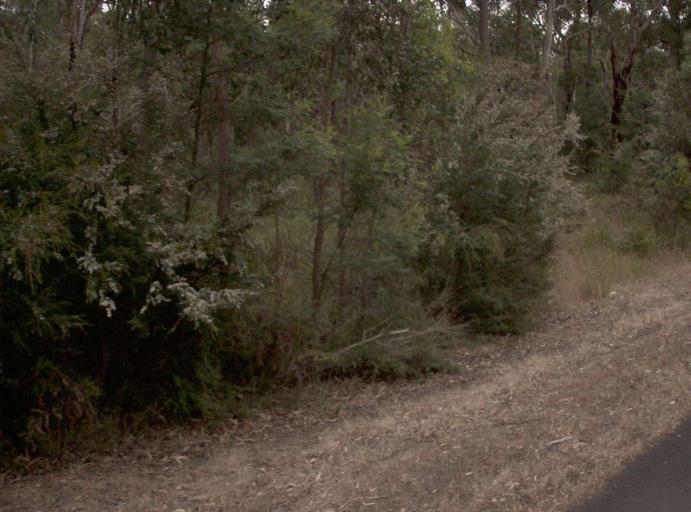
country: AU
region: Victoria
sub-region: Wellington
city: Sale
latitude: -38.4095
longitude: 146.9643
